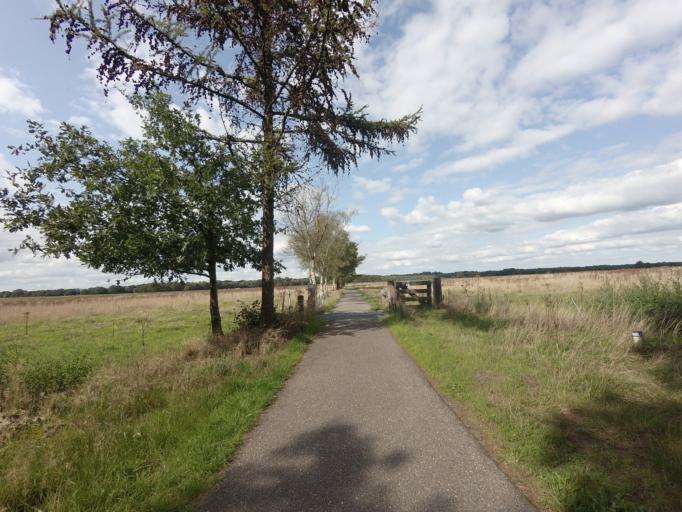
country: NL
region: Drenthe
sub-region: Gemeente De Wolden
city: Ruinen
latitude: 52.7952
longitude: 6.3545
